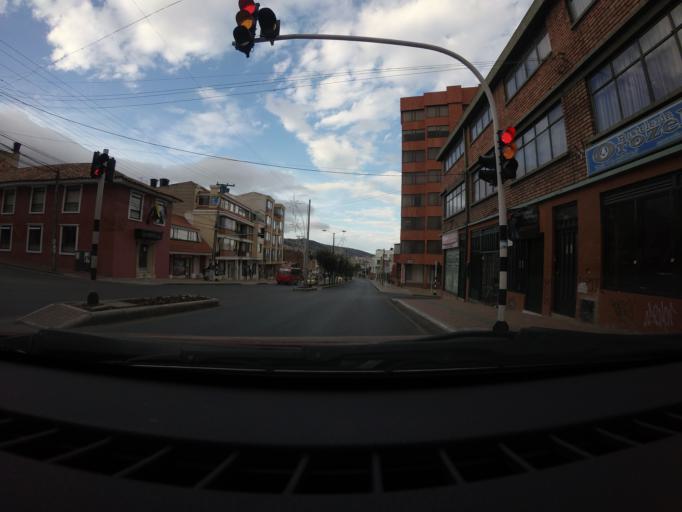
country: CO
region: Boyaca
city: Tunja
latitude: 5.5410
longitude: -73.3594
